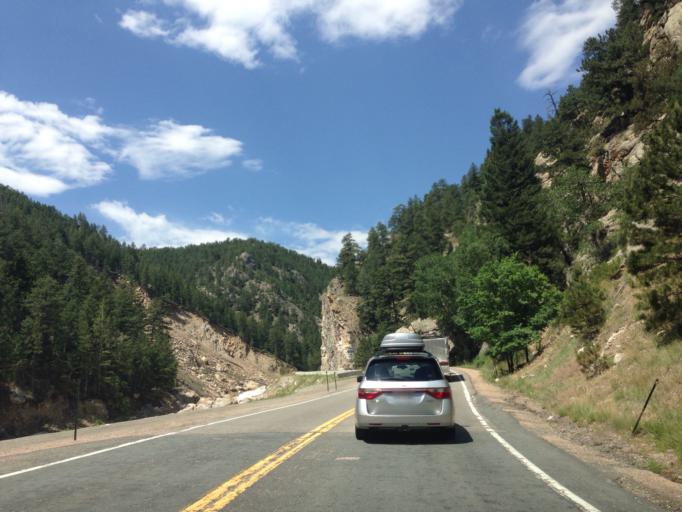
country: US
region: Colorado
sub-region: Larimer County
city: Estes Park
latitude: 40.4103
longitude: -105.3794
